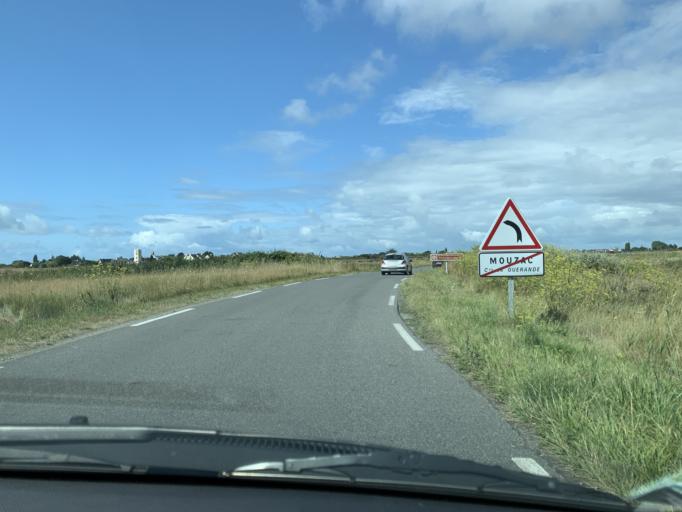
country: FR
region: Pays de la Loire
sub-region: Departement de la Loire-Atlantique
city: Le Pouliguen
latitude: 47.2977
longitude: -2.4186
